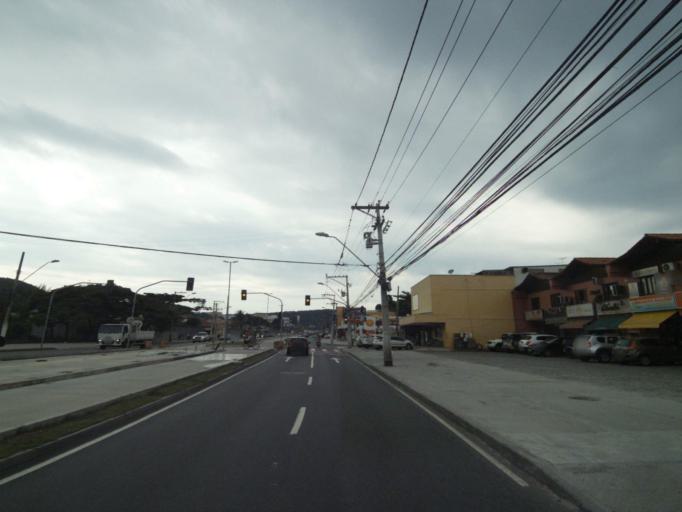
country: BR
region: Rio de Janeiro
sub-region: Niteroi
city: Niteroi
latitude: -22.9368
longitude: -43.0624
